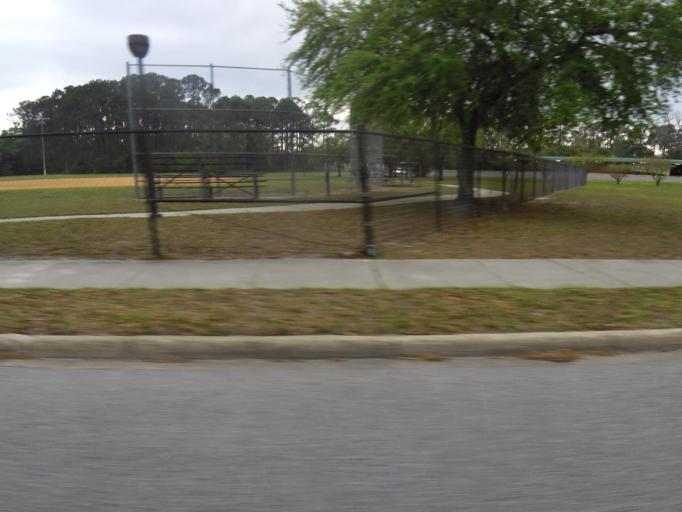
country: US
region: Florida
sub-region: Duval County
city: Jacksonville
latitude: 30.3020
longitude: -81.6339
